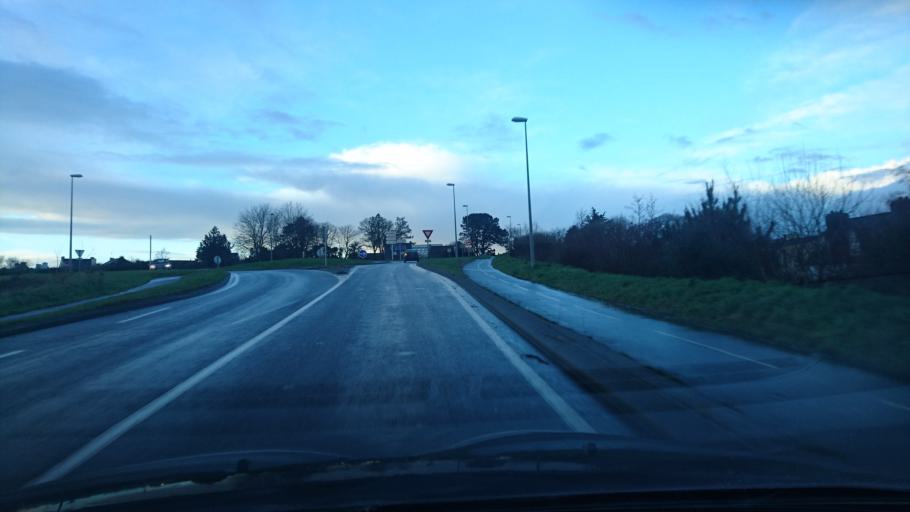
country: FR
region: Brittany
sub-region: Departement du Finistere
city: Guilers
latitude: 48.4183
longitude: -4.5594
